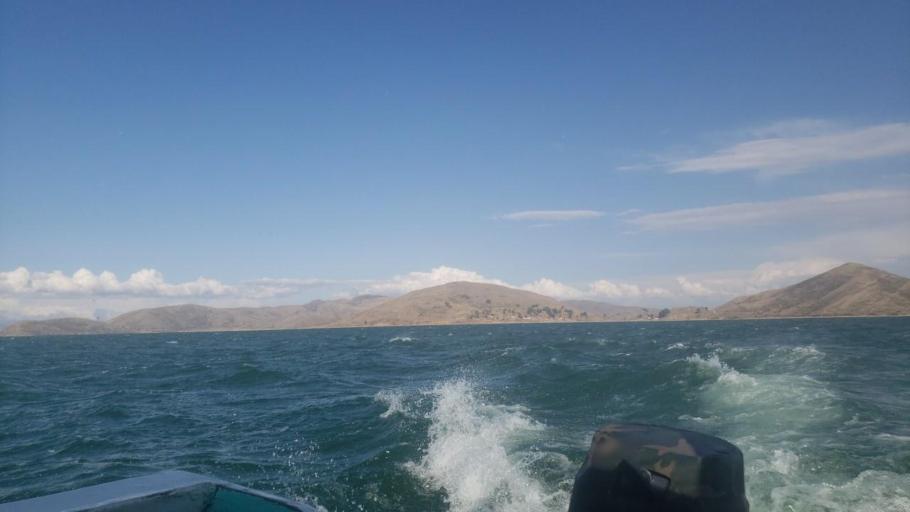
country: BO
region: La Paz
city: Huatajata
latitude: -16.3168
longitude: -68.7409
